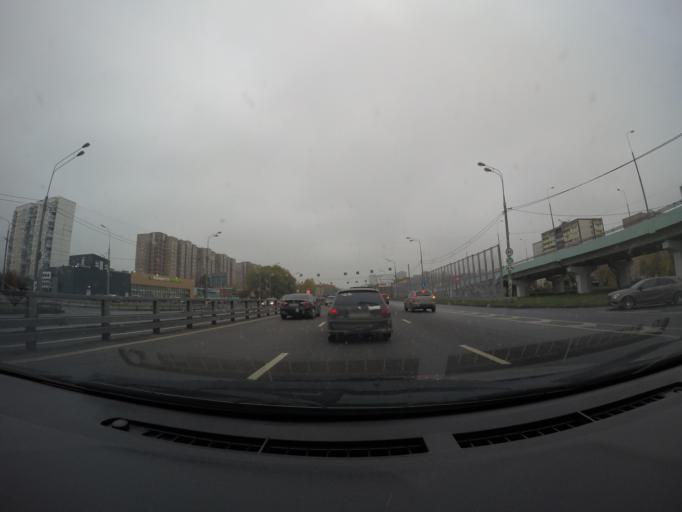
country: RU
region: Moskovskaya
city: Shcherbinka
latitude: 55.5345
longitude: 37.5821
